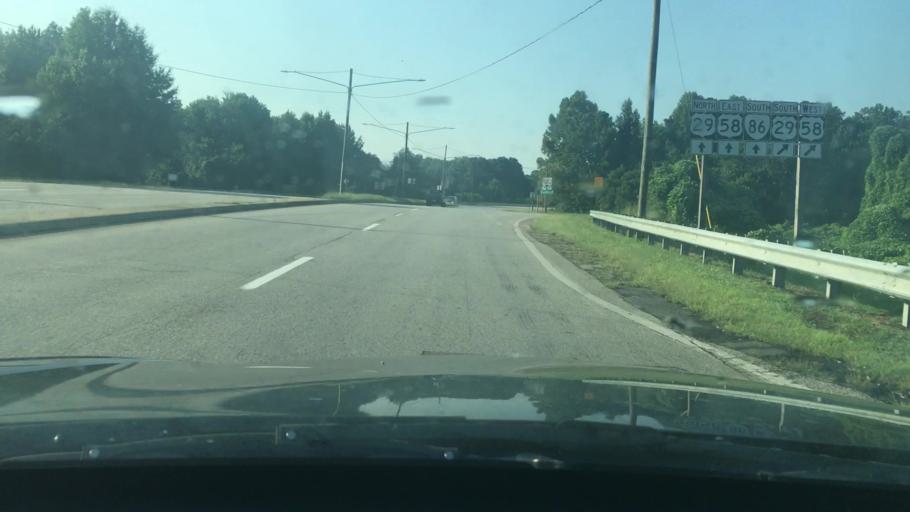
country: US
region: Virginia
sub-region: City of Danville
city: Danville
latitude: 36.5497
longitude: -79.4008
